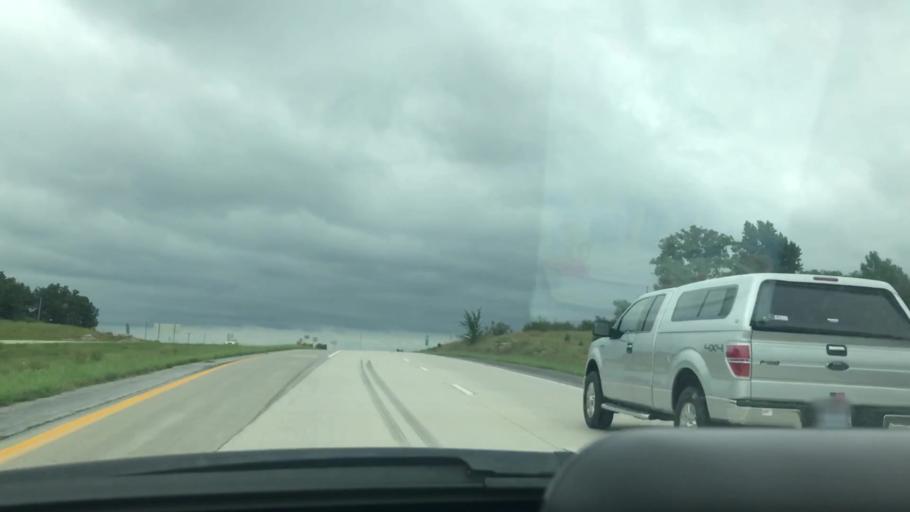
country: US
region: Missouri
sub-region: Greene County
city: Fair Grove
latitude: 37.4244
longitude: -93.1450
